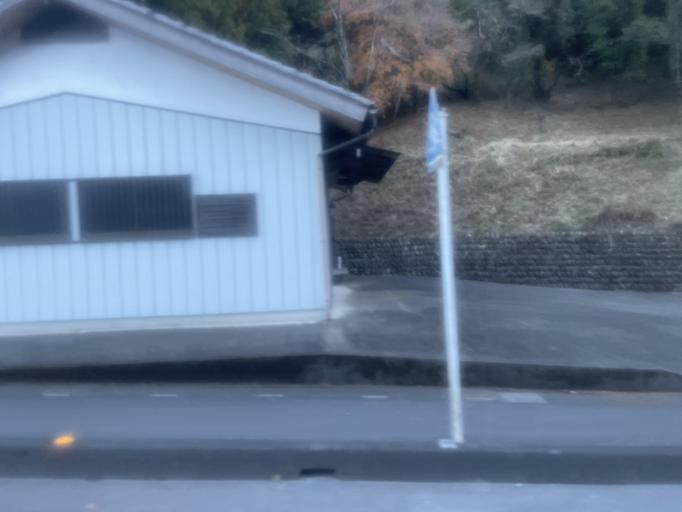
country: JP
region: Saitama
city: Yorii
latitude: 36.0762
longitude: 139.1782
